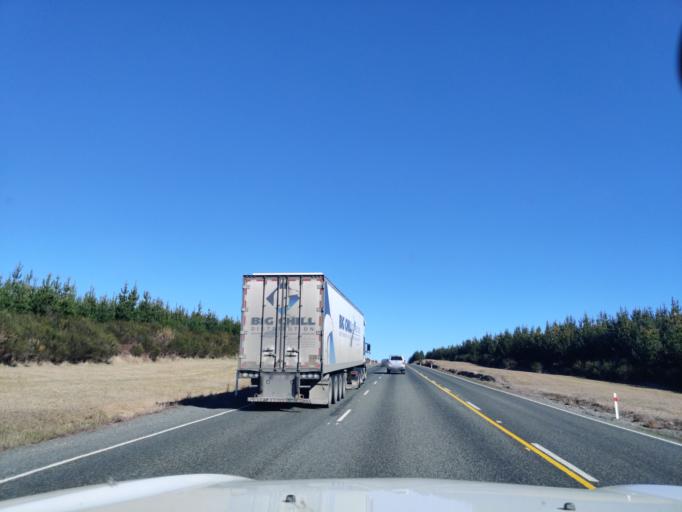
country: NZ
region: Waikato
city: Turangi
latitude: -39.1302
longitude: 175.7894
